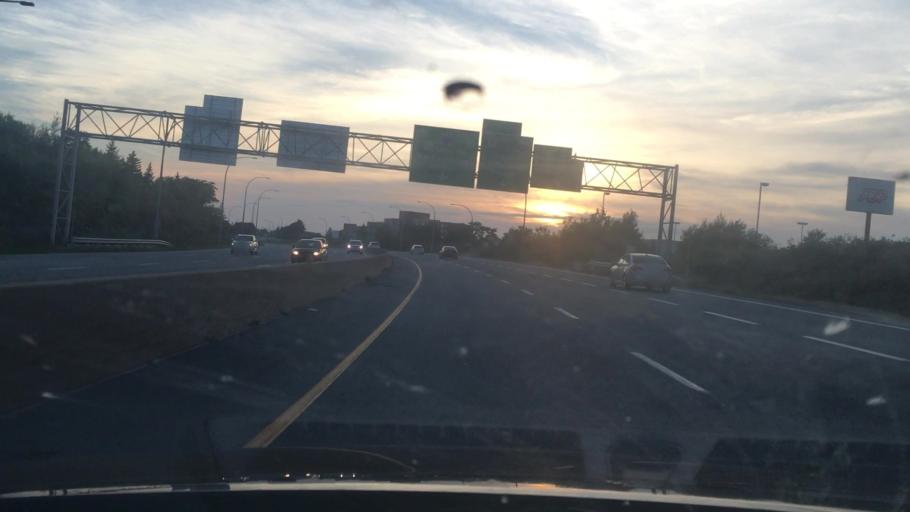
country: CA
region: Nova Scotia
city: Dartmouth
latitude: 44.6943
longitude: -63.5726
